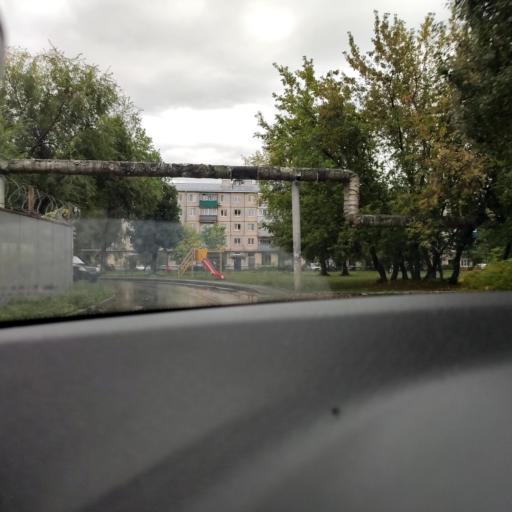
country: RU
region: Samara
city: Novosemeykino
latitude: 53.3480
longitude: 50.2278
